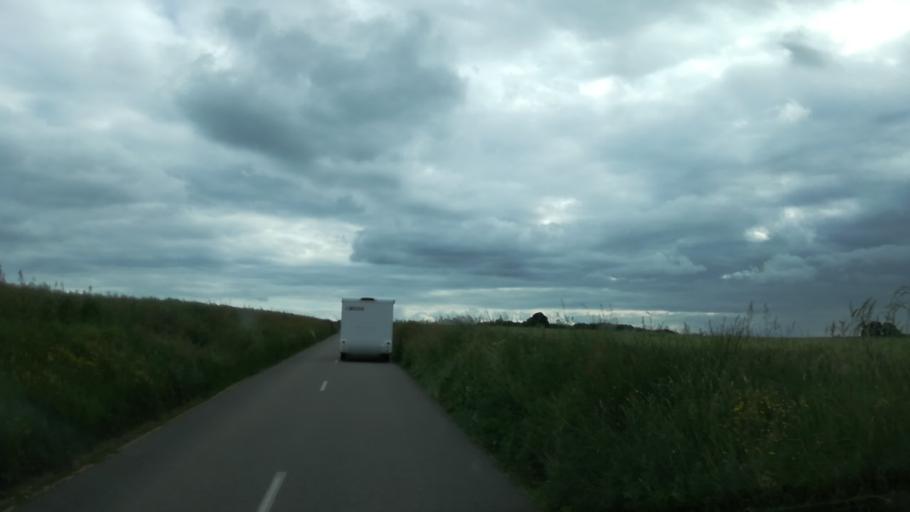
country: FR
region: Haute-Normandie
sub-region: Departement de l'Eure
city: Bourg-Achard
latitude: 49.3410
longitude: 0.8147
